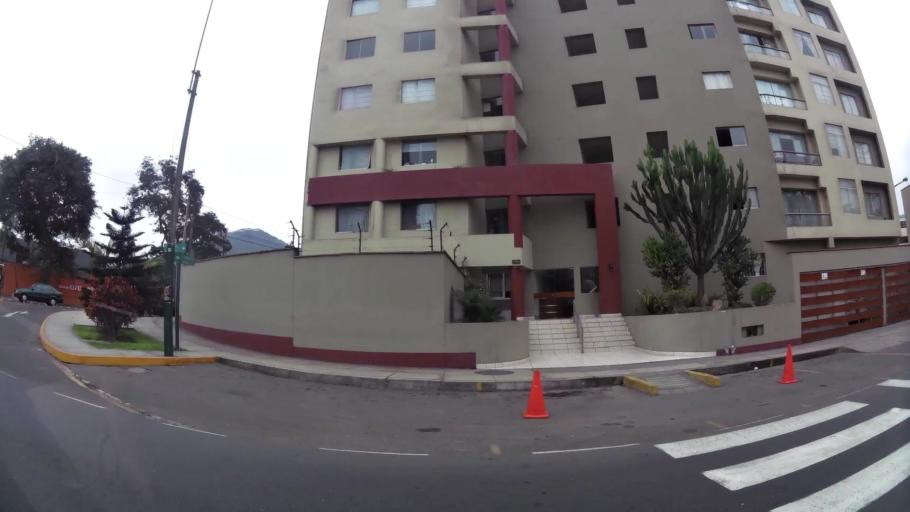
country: PE
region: Lima
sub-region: Lima
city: La Molina
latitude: -12.1039
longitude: -76.9704
